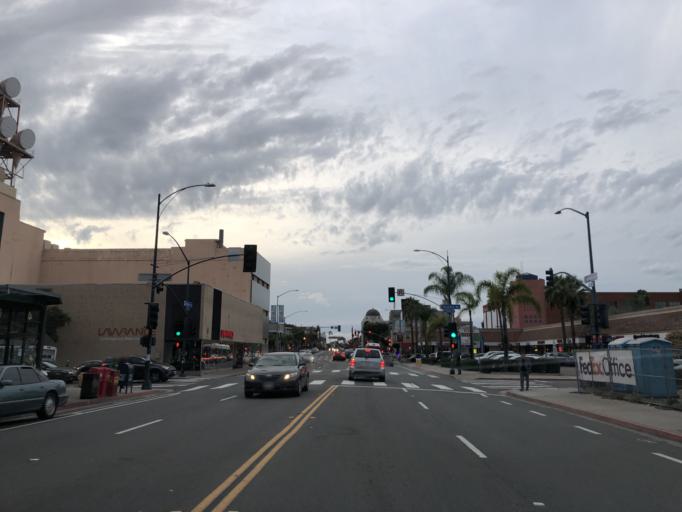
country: US
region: California
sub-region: San Diego County
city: San Diego
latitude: 32.7484
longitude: -117.1581
